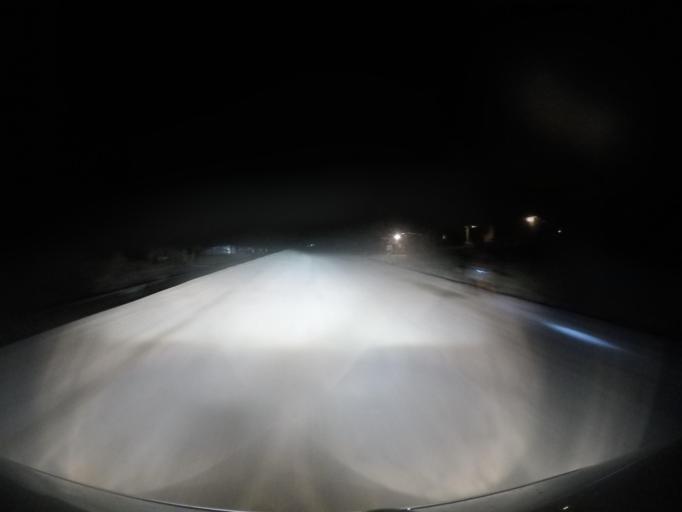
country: TL
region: Viqueque
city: Viqueque
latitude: -8.8074
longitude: 126.5430
